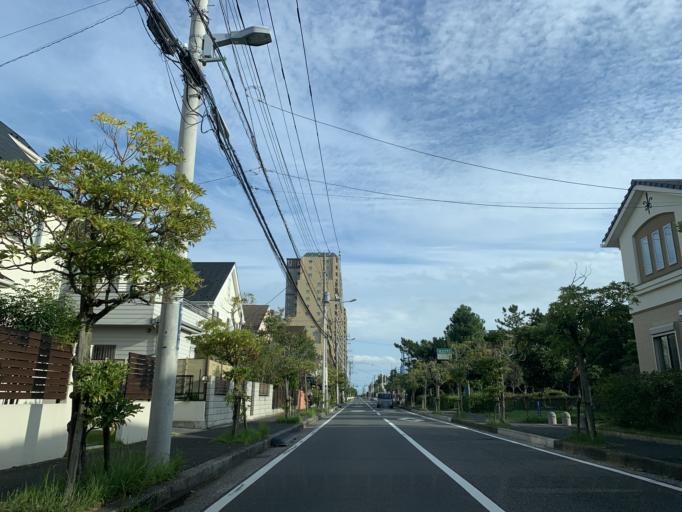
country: JP
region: Tokyo
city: Urayasu
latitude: 35.6360
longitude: 139.9118
